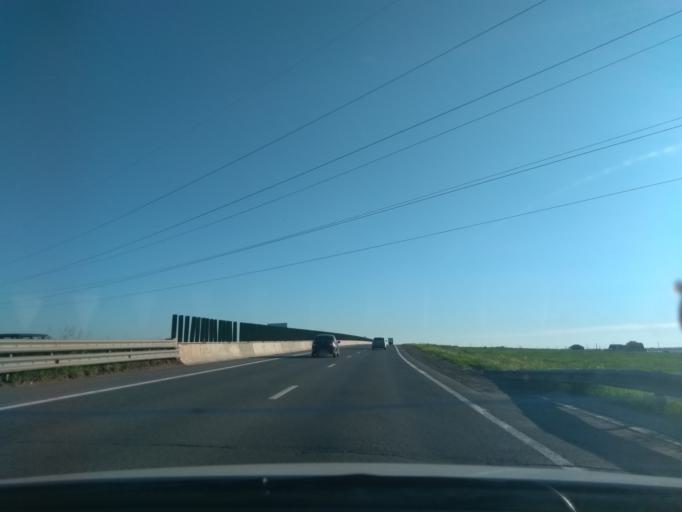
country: RU
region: Perm
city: Ferma
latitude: 57.9375
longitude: 56.3644
